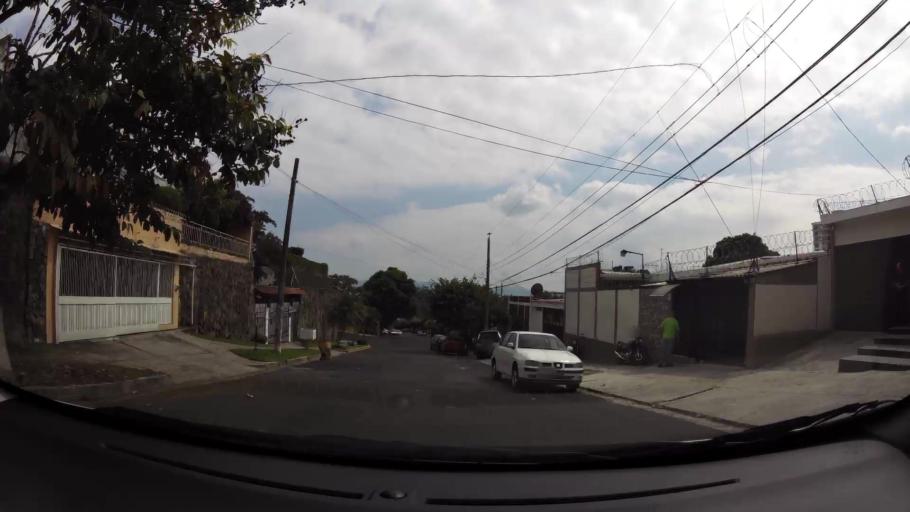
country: SV
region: La Libertad
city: Santa Tecla
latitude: 13.7061
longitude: -89.2529
